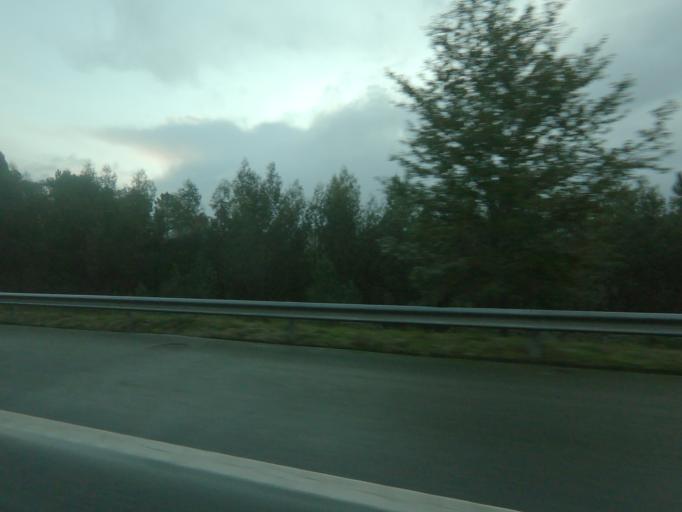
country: PT
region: Braga
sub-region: Barcelos
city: Galegos
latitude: 41.6413
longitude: -8.5573
